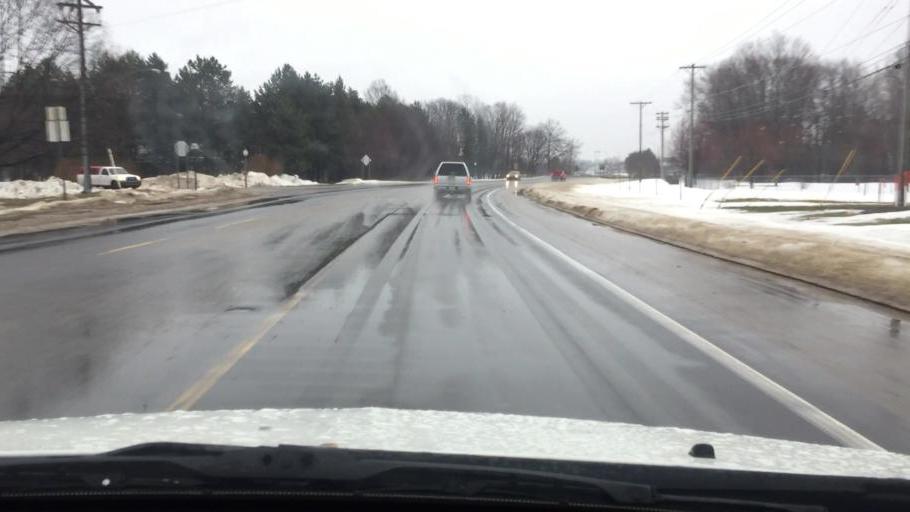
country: US
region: Michigan
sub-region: Charlevoix County
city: Charlevoix
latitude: 45.3024
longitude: -85.2589
